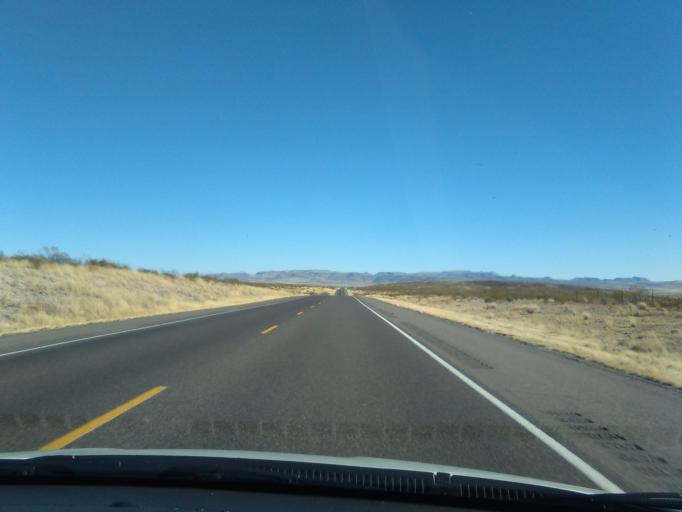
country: US
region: New Mexico
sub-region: Dona Ana County
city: Hatch
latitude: 32.5760
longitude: -107.4281
